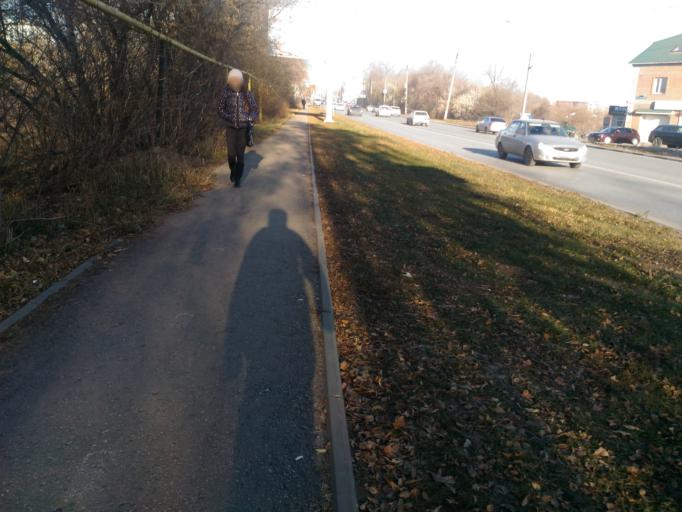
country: RU
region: Ulyanovsk
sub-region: Ulyanovskiy Rayon
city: Ulyanovsk
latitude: 54.3131
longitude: 48.3788
